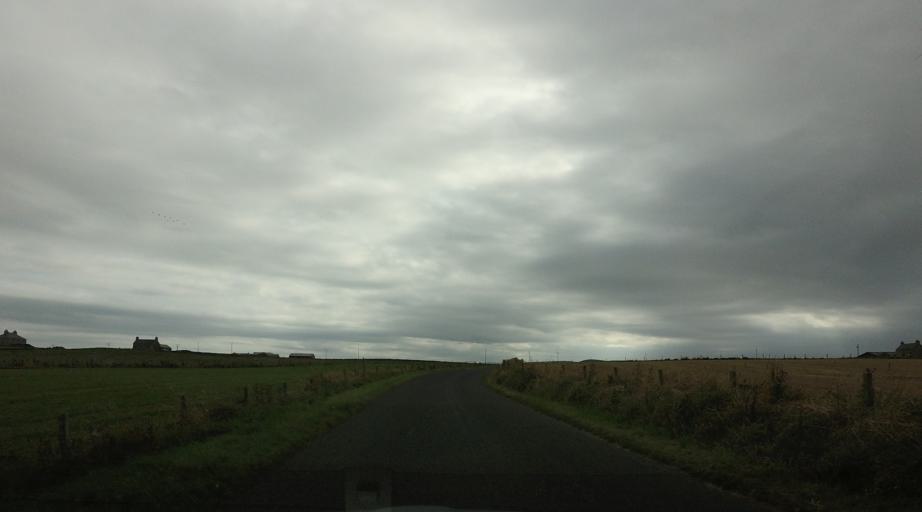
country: GB
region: Scotland
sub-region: Orkney Islands
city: Stromness
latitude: 59.0391
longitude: -3.3110
